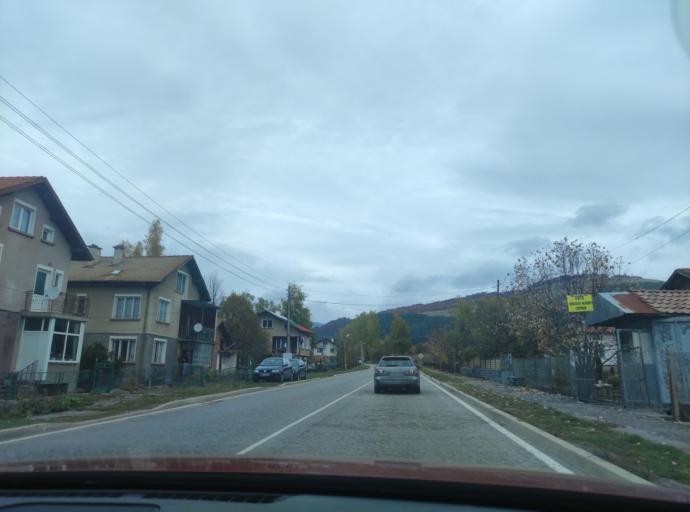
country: BG
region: Sofiya
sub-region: Obshtina Godech
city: Godech
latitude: 43.0770
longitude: 23.1076
